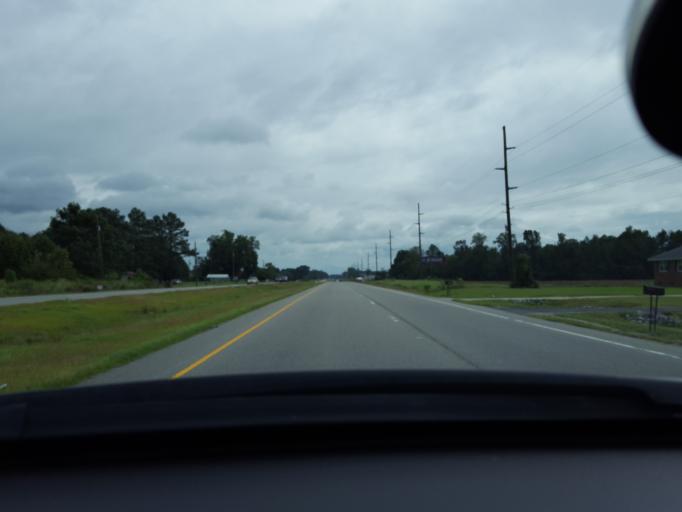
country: US
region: North Carolina
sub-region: Pitt County
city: Ayden
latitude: 35.4390
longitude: -77.4329
